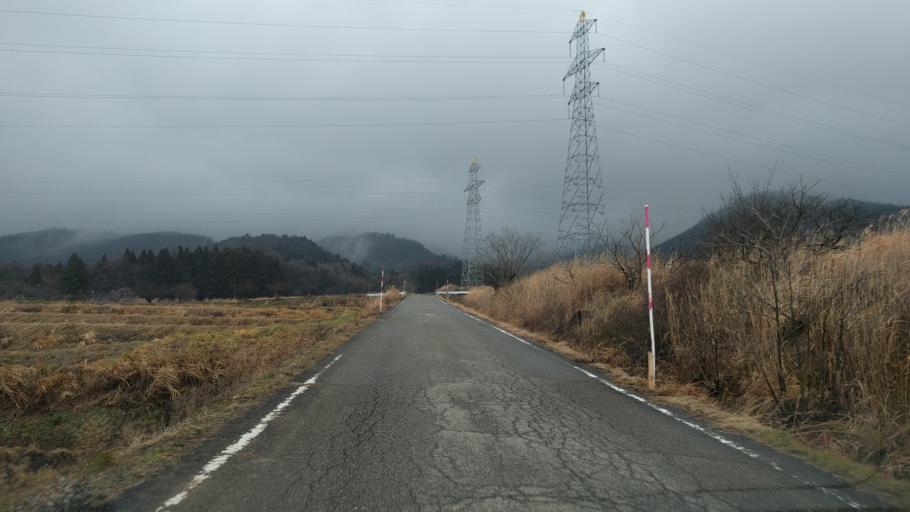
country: JP
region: Fukushima
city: Kitakata
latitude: 37.5759
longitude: 139.9608
